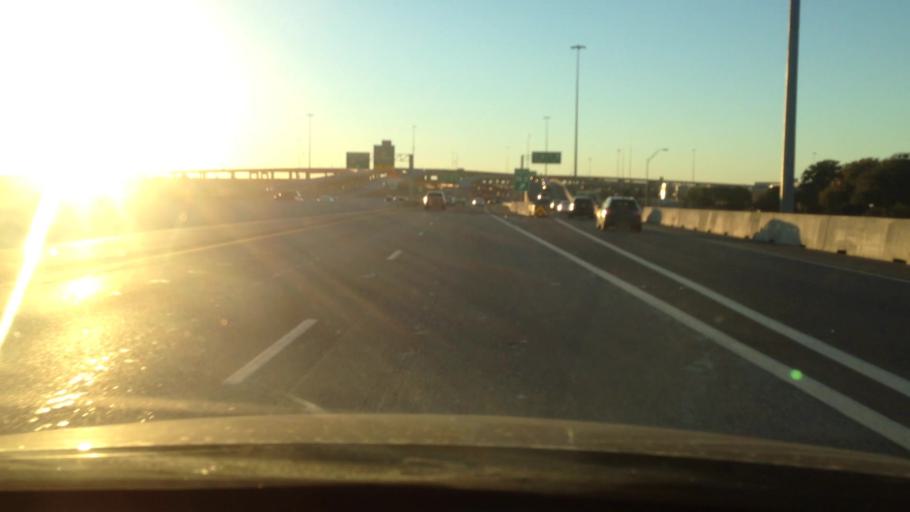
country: US
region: Texas
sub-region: Tarrant County
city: Blue Mound
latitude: 32.8396
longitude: -97.3011
